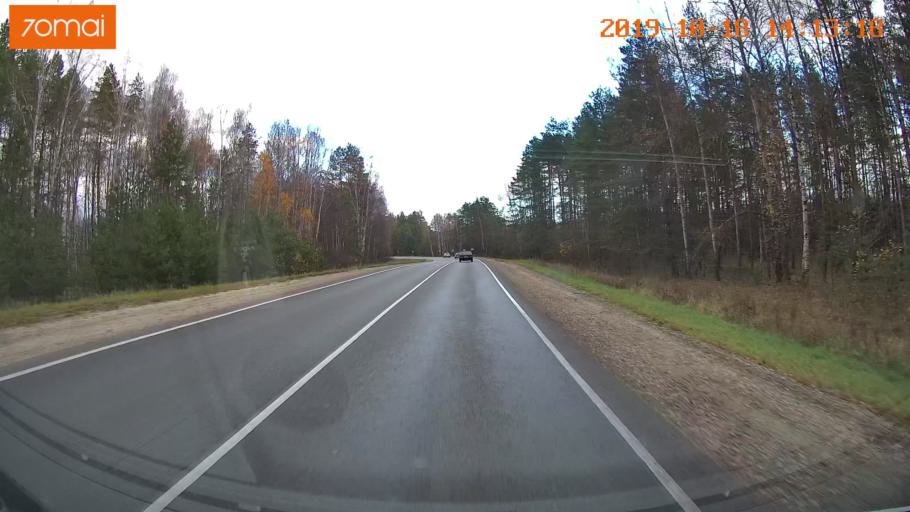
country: RU
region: Rjazan
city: Spas-Klepiki
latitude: 55.1510
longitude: 40.2697
